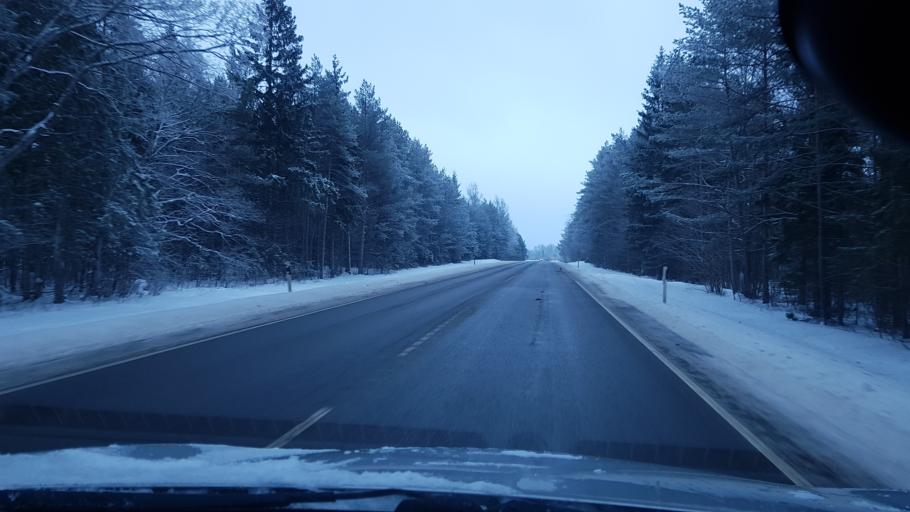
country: EE
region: Harju
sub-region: Keila linn
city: Keila
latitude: 59.3308
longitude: 24.2952
